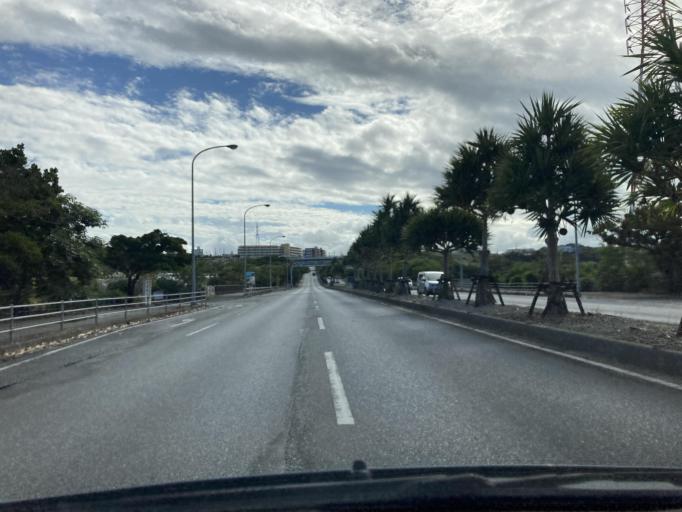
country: JP
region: Okinawa
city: Tomigusuku
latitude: 26.1695
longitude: 127.7263
